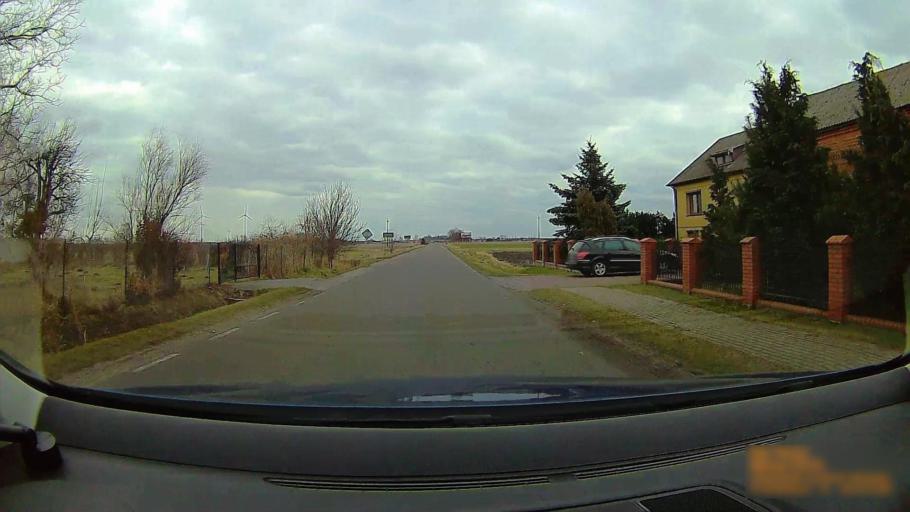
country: PL
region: Greater Poland Voivodeship
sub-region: Powiat koninski
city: Rychwal
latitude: 52.0974
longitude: 18.1175
